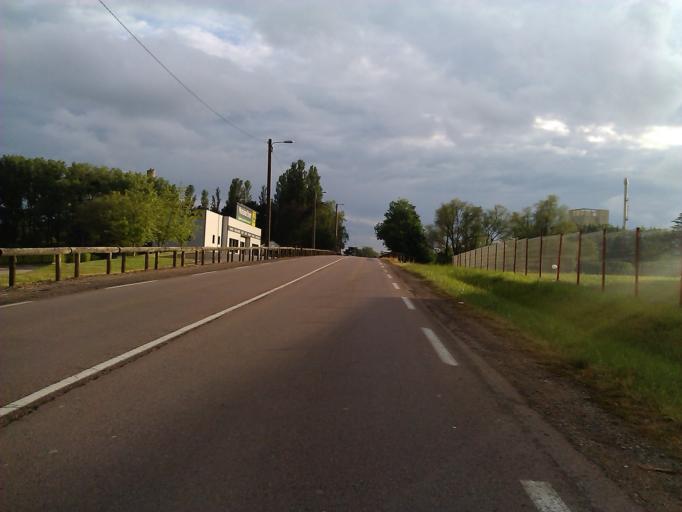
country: FR
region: Bourgogne
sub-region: Departement de Saone-et-Loire
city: Crissey
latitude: 46.8094
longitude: 4.8649
